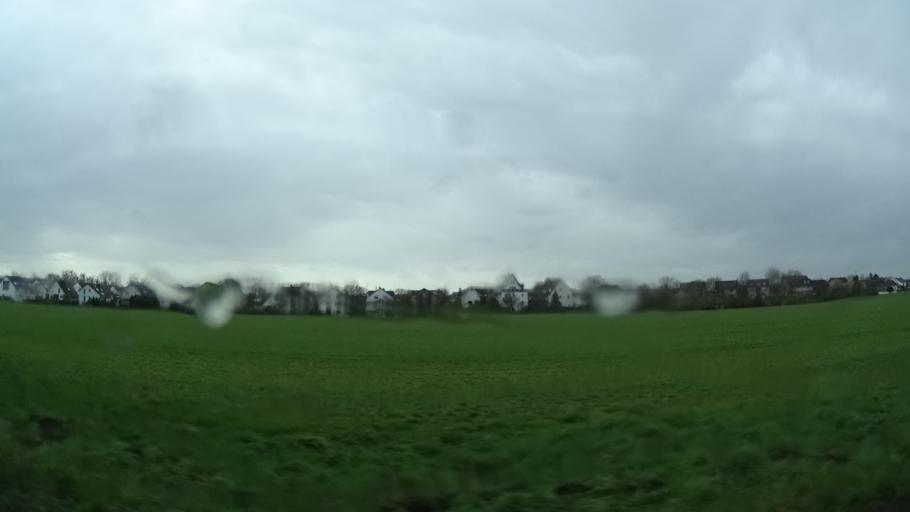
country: DE
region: Hesse
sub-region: Regierungsbezirk Darmstadt
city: Riedstadt
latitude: 49.8312
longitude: 8.4812
